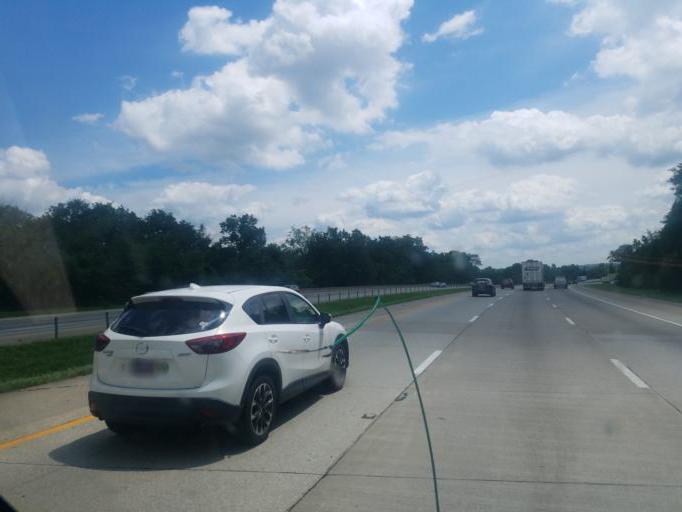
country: US
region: Kentucky
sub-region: Bullitt County
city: Shepherdsville
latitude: 38.0141
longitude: -85.6967
